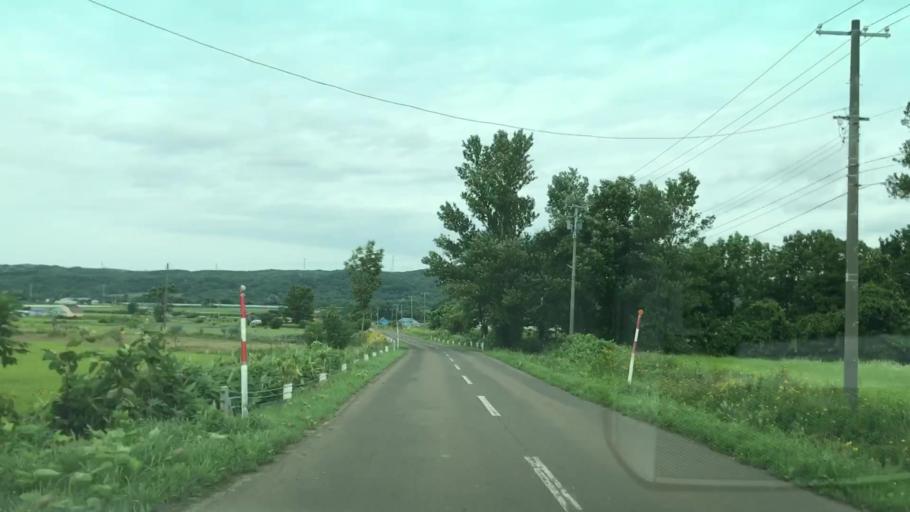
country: JP
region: Hokkaido
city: Iwanai
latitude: 43.0333
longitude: 140.5657
